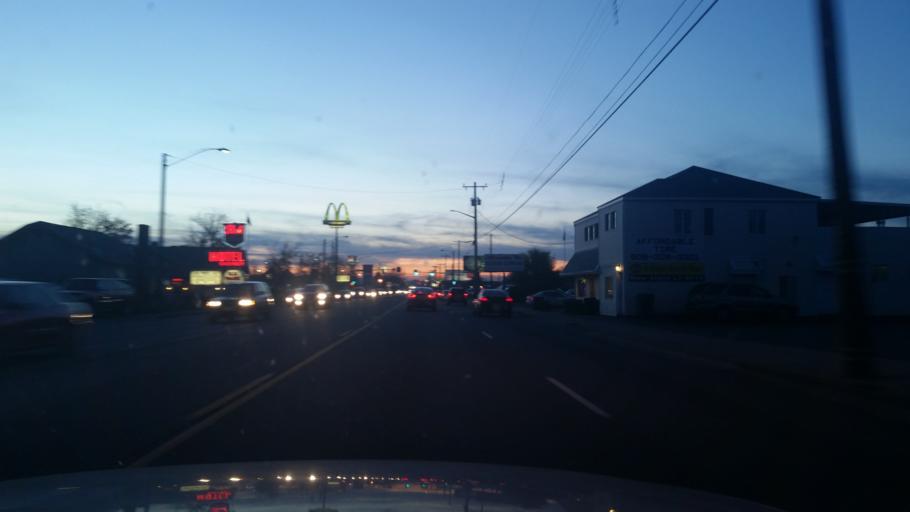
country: US
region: Washington
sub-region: Spokane County
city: Millwood
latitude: 47.6573
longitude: -117.3444
